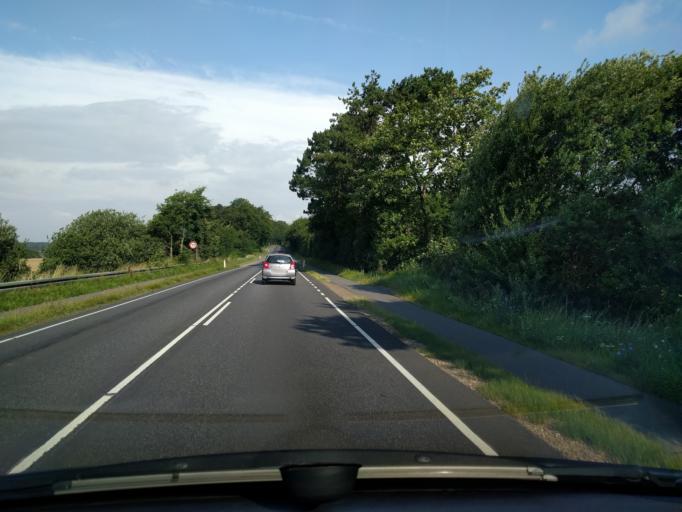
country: DK
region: Zealand
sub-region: Naestved Kommune
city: Naestved
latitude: 55.1894
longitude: 11.8537
